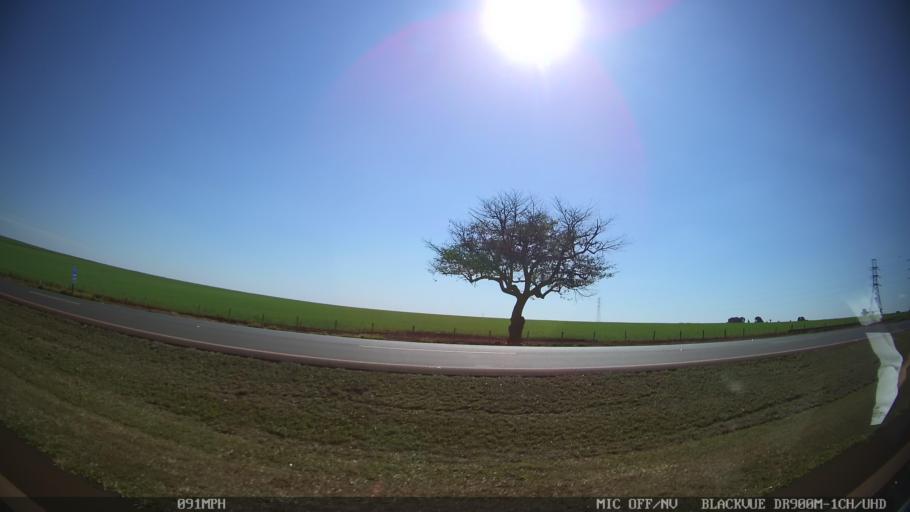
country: BR
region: Sao Paulo
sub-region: Ribeirao Preto
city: Ribeirao Preto
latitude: -21.1536
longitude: -47.8903
